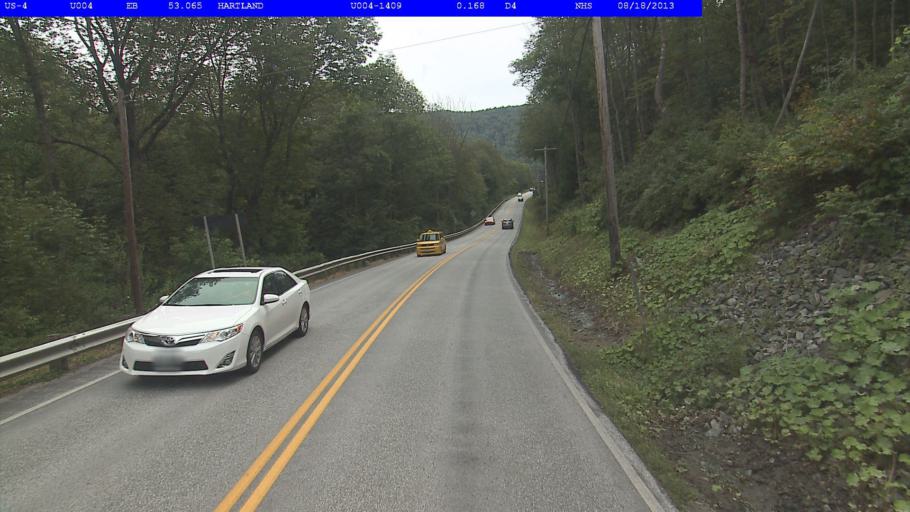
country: US
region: Vermont
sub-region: Windsor County
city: Woodstock
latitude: 43.6289
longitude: -72.4650
